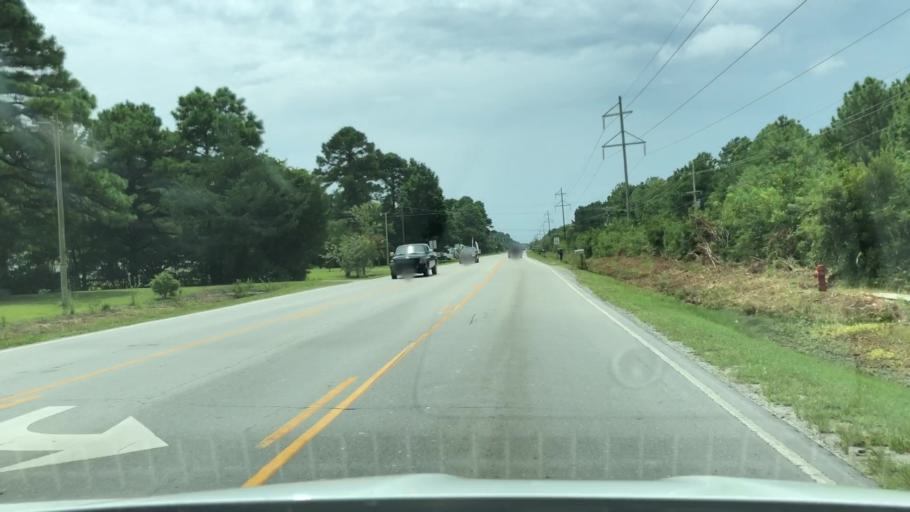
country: US
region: North Carolina
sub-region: Carteret County
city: Newport
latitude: 34.7546
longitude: -76.8753
